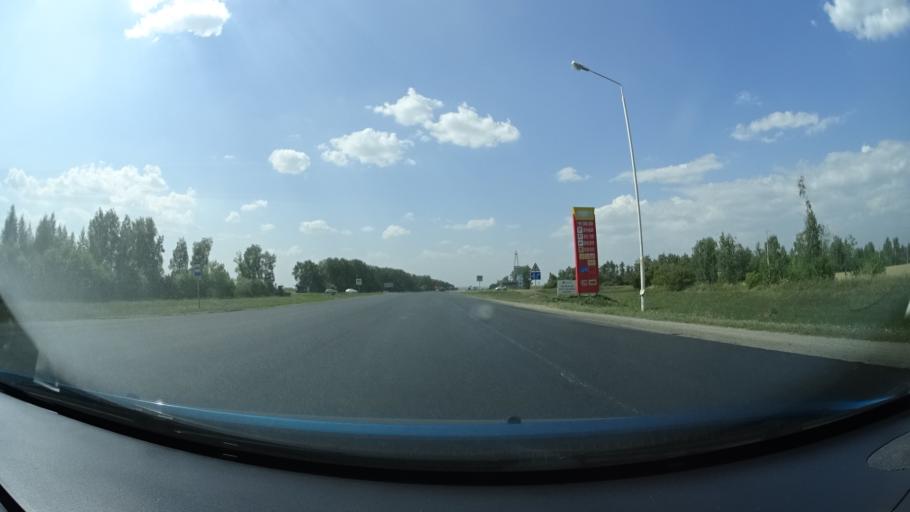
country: RU
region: Bashkortostan
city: Kandry
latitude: 54.5400
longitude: 54.1339
